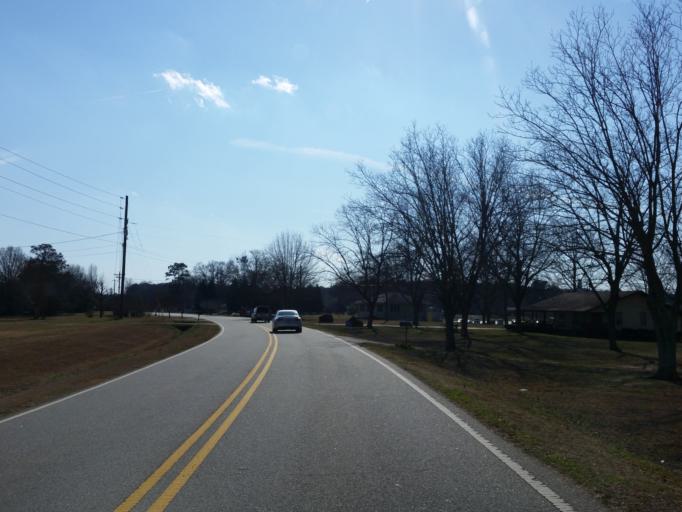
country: US
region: Georgia
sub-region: Clayton County
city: Lovejoy
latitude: 33.4345
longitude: -84.2740
